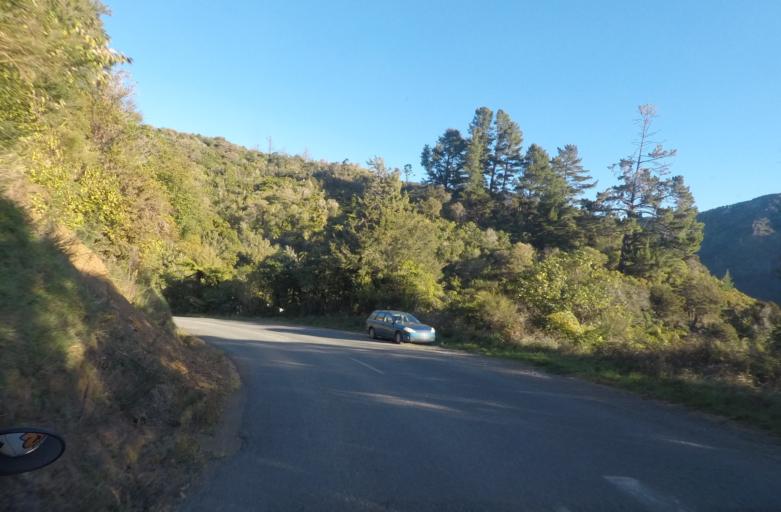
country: NZ
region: Marlborough
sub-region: Marlborough District
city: Picton
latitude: -41.2728
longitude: 173.9697
